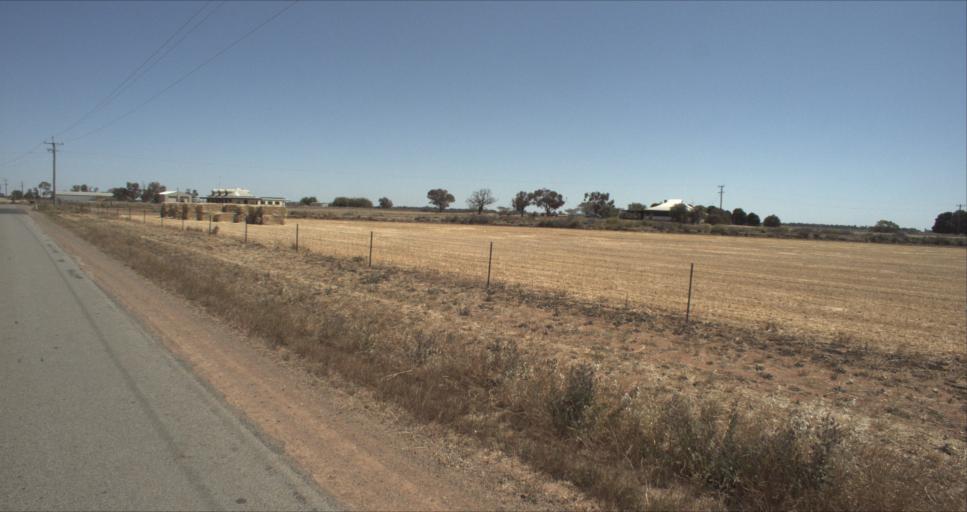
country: AU
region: New South Wales
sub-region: Leeton
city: Leeton
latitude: -34.5349
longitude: 146.4457
